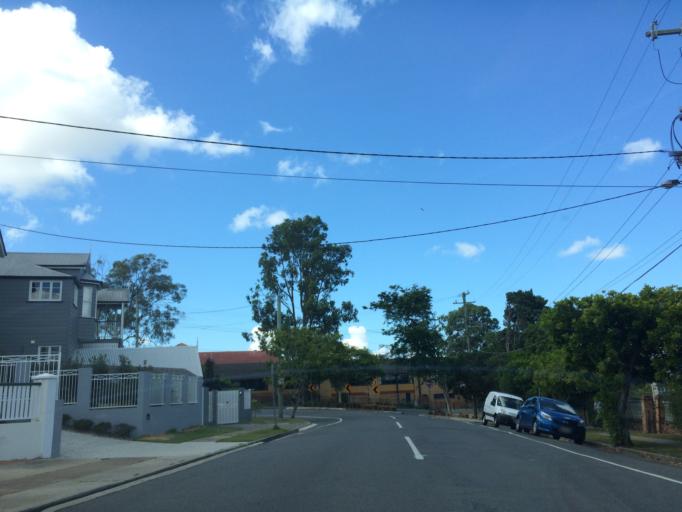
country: AU
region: Queensland
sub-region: Brisbane
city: Woolloongabba
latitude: -27.4852
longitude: 153.0506
